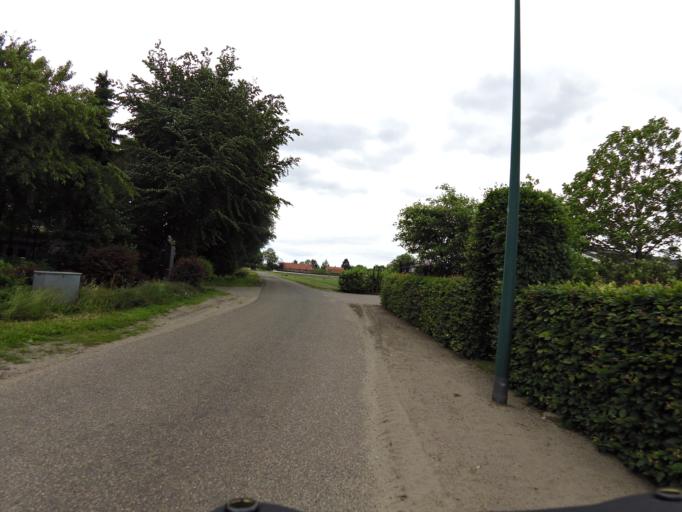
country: NL
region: North Brabant
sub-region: Gemeente Breda
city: Breda
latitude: 51.5250
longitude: 4.7221
